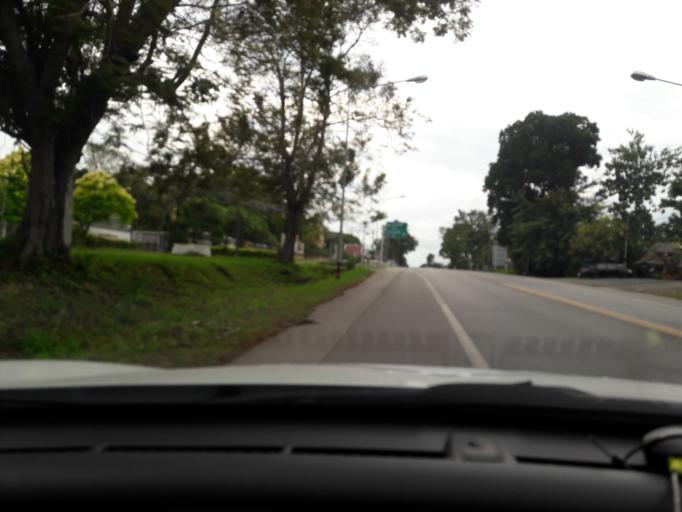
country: TH
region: Nakhon Sawan
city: Tak Fa
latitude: 15.3493
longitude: 100.4986
